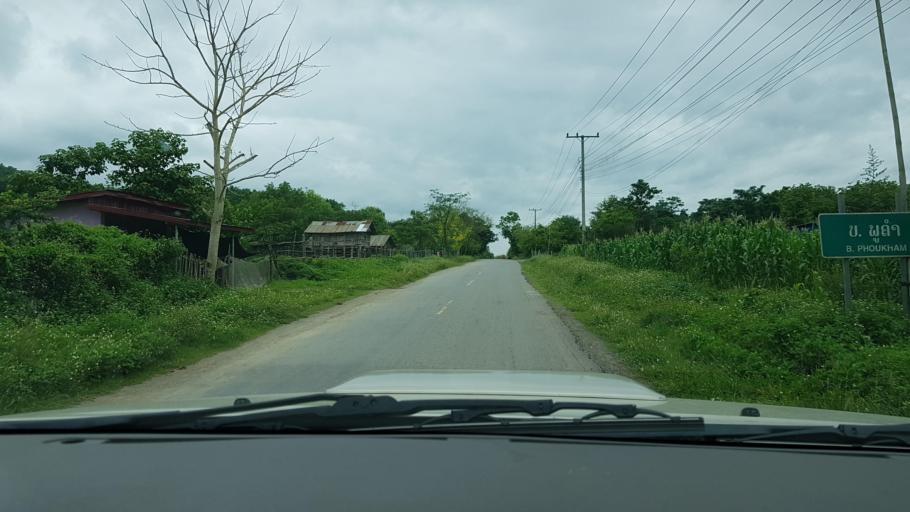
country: LA
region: Loungnamtha
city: Muang Nale
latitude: 20.2672
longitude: 101.5977
